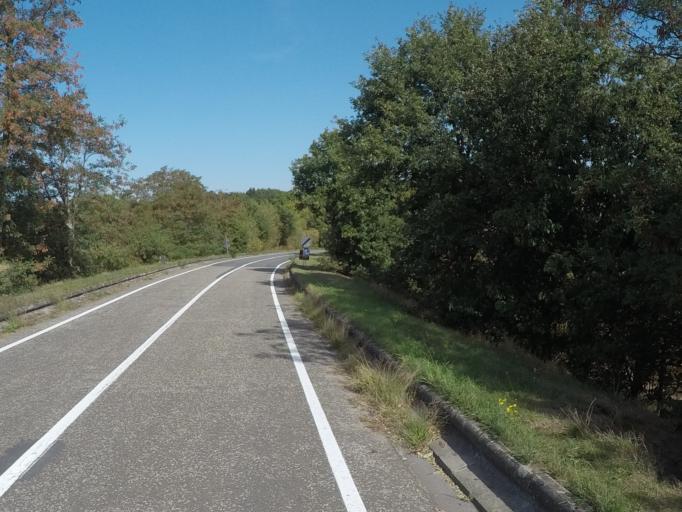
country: BE
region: Flanders
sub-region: Provincie Antwerpen
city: Zoersel
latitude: 51.2446
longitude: 4.7207
